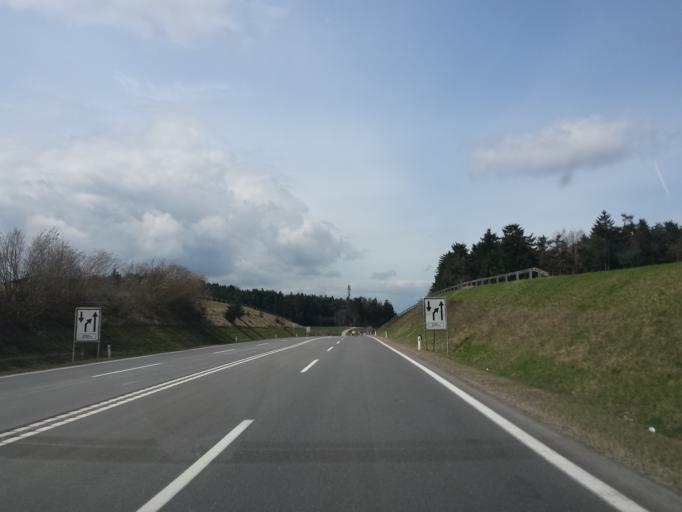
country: AT
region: Lower Austria
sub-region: Politischer Bezirk Krems
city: Rastenfeld
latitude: 48.5373
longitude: 15.3815
